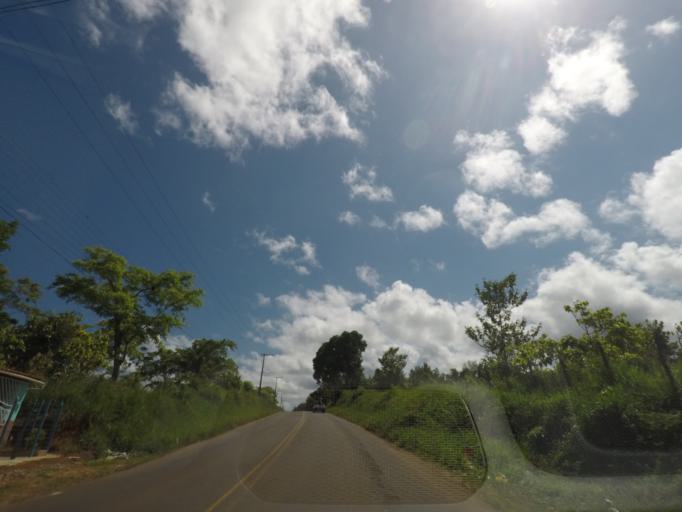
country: BR
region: Bahia
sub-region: Taperoa
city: Taperoa
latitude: -13.5261
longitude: -39.1039
